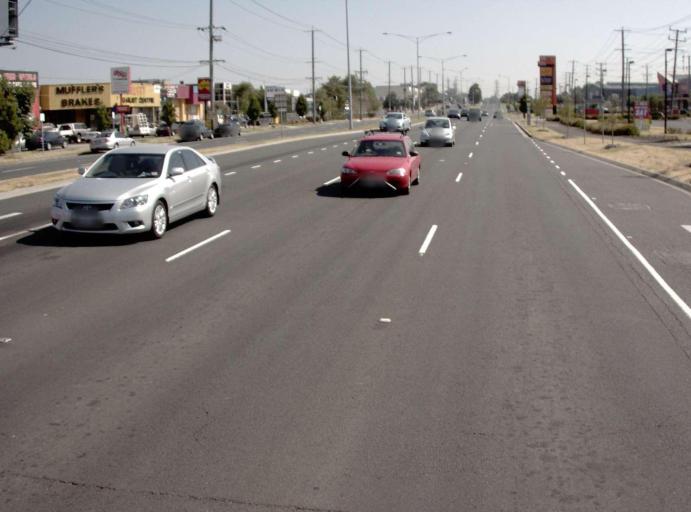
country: AU
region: Victoria
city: Highett
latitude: -37.9494
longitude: 145.0777
